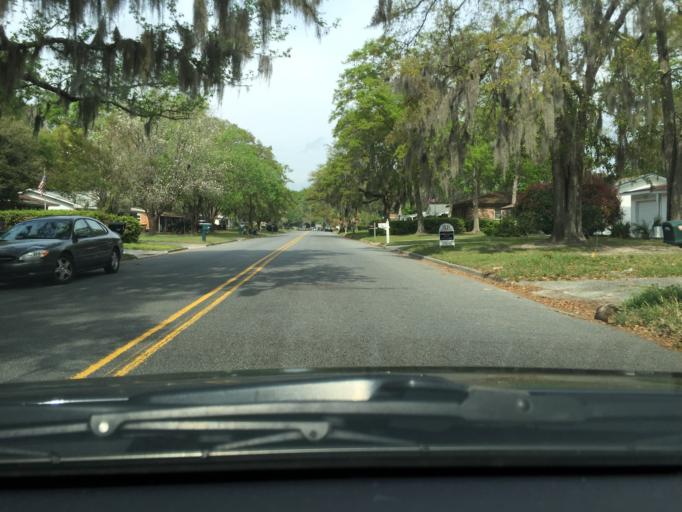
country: US
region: Georgia
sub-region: Chatham County
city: Montgomery
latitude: 31.9860
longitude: -81.1418
